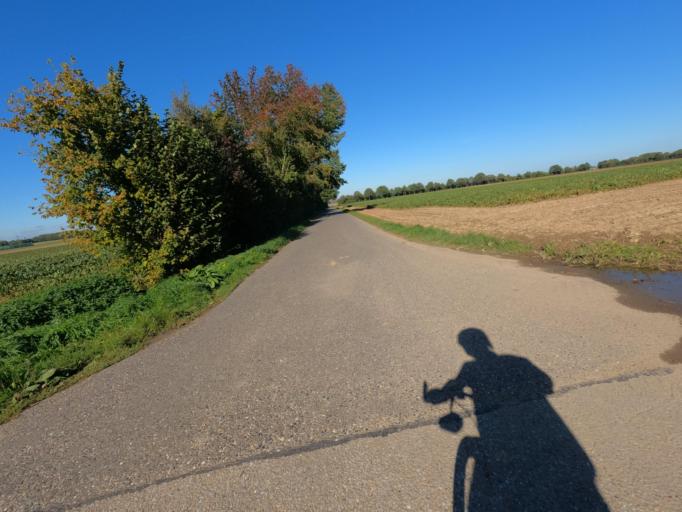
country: DE
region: North Rhine-Westphalia
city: Erkelenz
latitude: 51.0651
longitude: 6.3450
